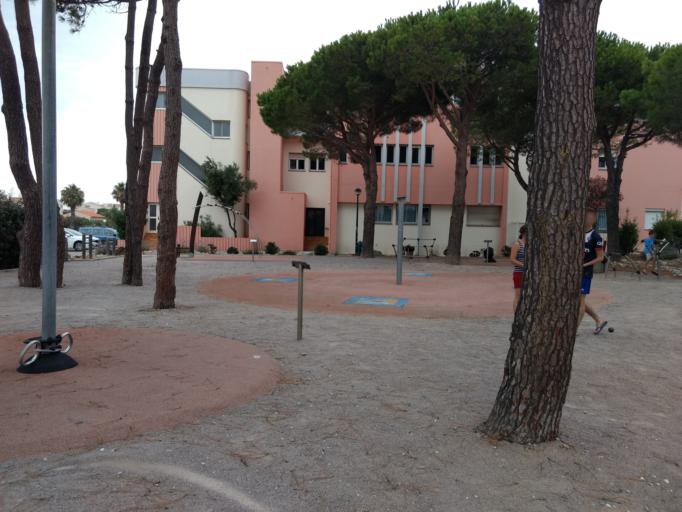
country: FR
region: Languedoc-Roussillon
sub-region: Departement des Pyrenees-Orientales
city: Le Barcares
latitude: 42.7888
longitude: 3.0346
